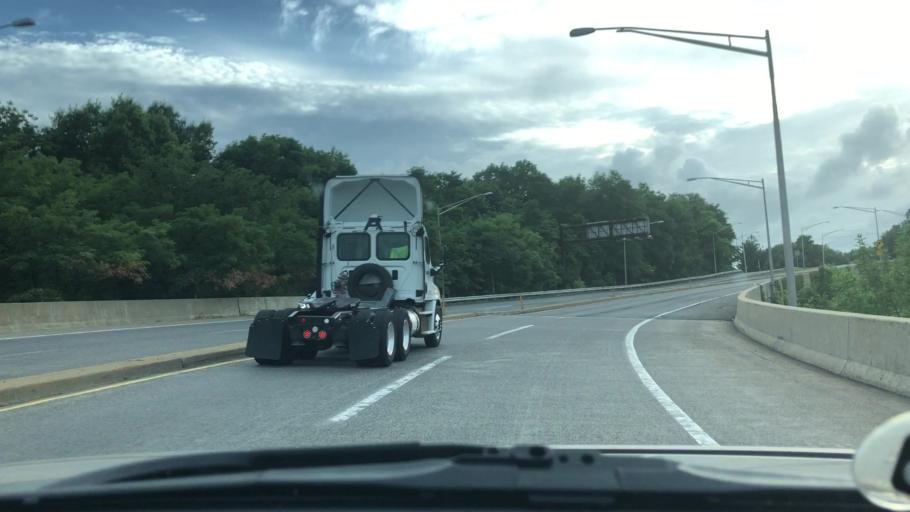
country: US
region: New Jersey
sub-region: Burlington County
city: Bordentown
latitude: 40.1234
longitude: -74.7028
